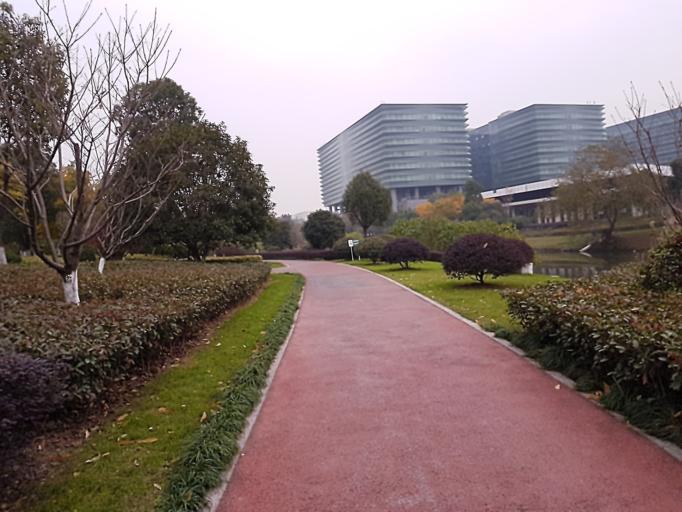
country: CN
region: Zhejiang Sheng
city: Cangqian
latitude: 30.2859
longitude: 120.0112
